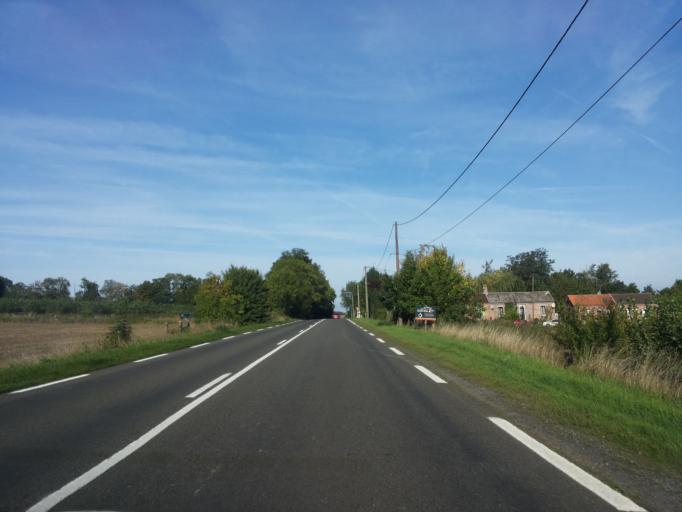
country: FR
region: Picardie
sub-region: Departement de l'Aisne
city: Charmes
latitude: 49.6293
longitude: 3.4278
